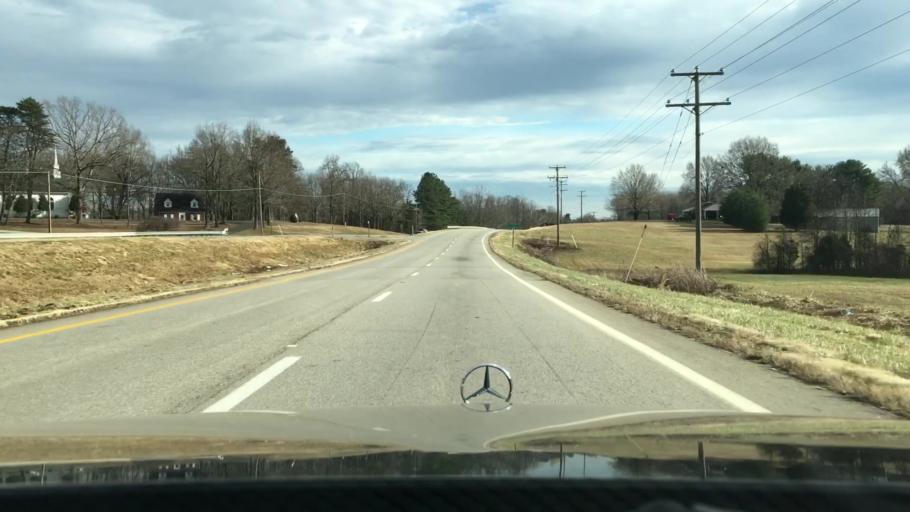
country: US
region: Virginia
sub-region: Pittsylvania County
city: Mount Hermon
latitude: 36.7192
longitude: -79.3822
